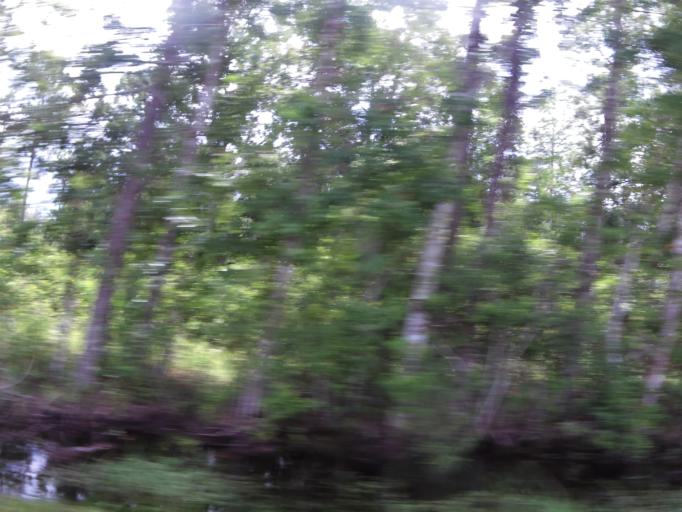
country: US
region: Florida
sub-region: Flagler County
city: Palm Coast
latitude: 29.6544
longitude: -81.3486
